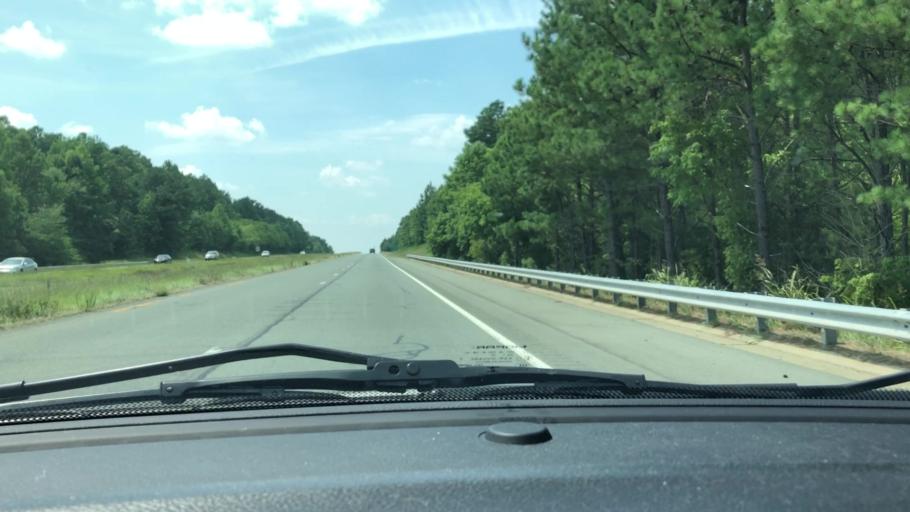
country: US
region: North Carolina
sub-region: Chatham County
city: Siler City
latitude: 35.7564
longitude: -79.4604
